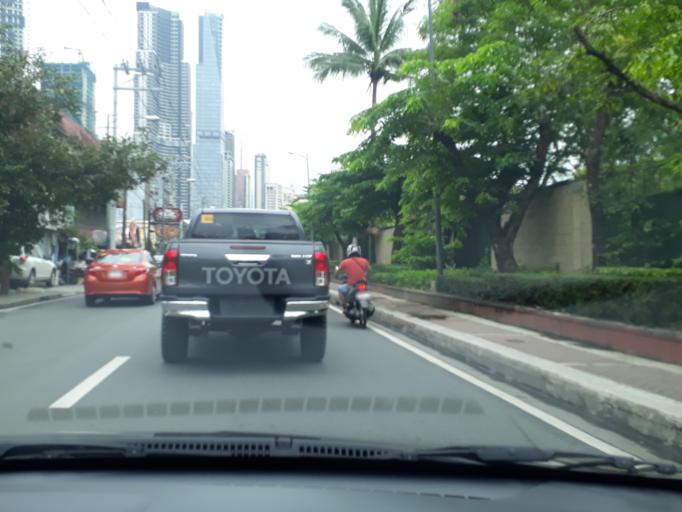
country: PH
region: Metro Manila
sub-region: Makati City
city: Makati City
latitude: 14.5674
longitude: 121.0214
